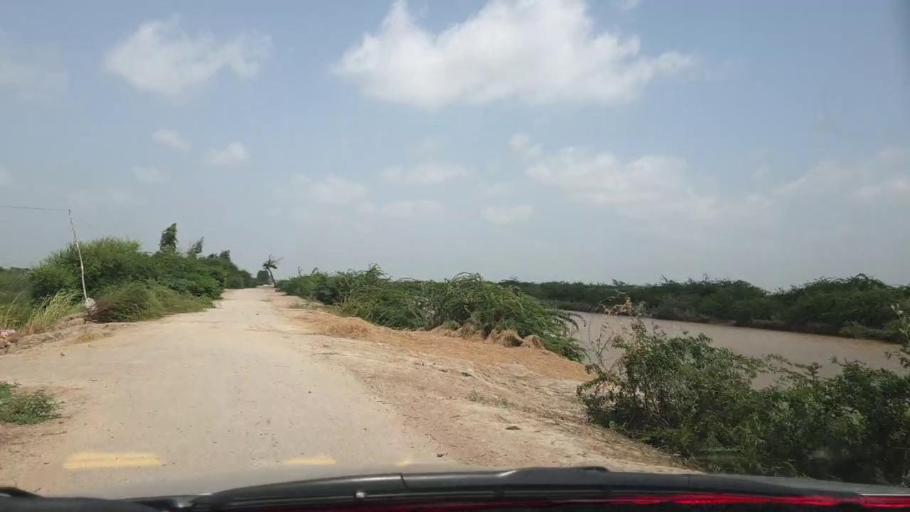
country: PK
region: Sindh
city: Talhar
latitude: 24.8907
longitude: 68.8351
